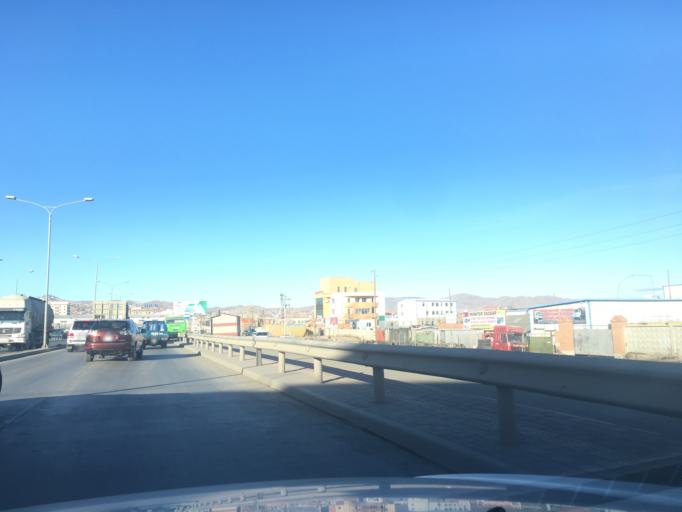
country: MN
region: Ulaanbaatar
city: Ulaanbaatar
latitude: 47.9051
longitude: 106.7861
